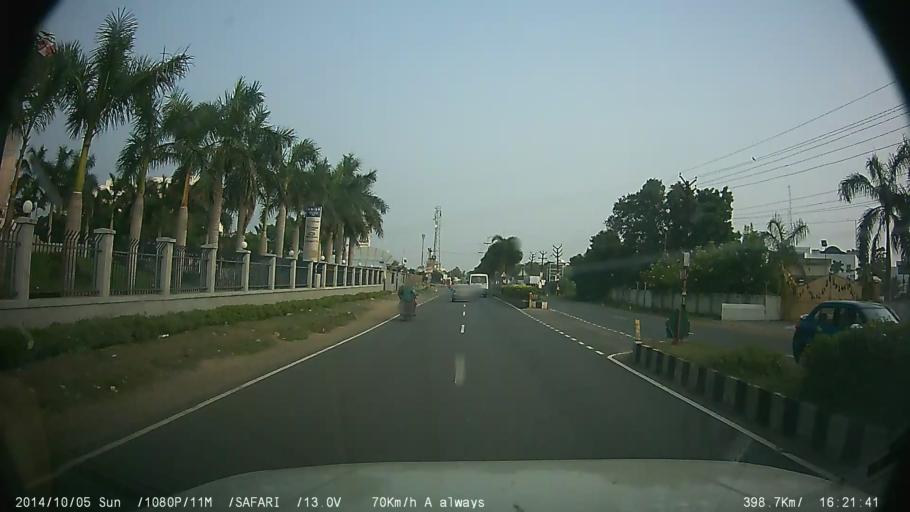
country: IN
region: Tamil Nadu
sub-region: Kancheepuram
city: Vengavasal
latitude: 12.8415
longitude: 80.1515
